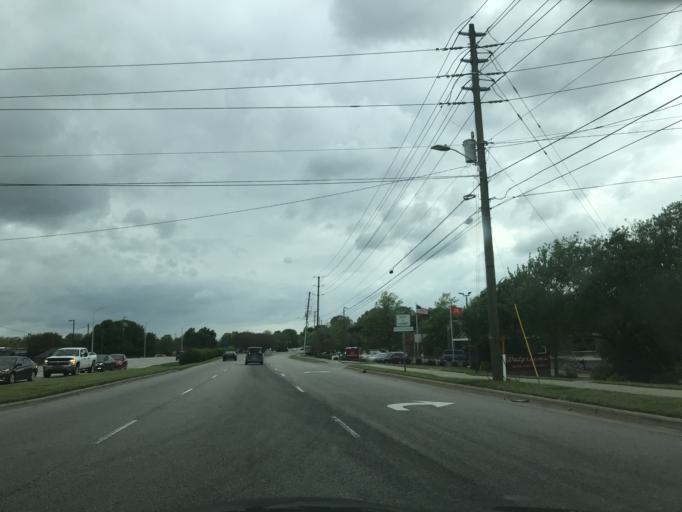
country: US
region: North Carolina
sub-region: Wake County
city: Knightdale
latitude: 35.7984
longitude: -78.4876
